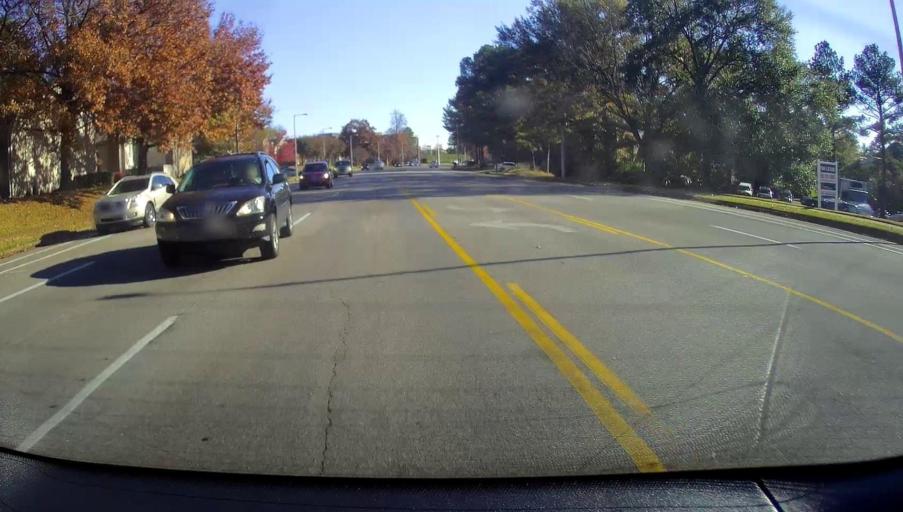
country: US
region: Tennessee
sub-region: Shelby County
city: Germantown
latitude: 35.1030
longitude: -89.8409
